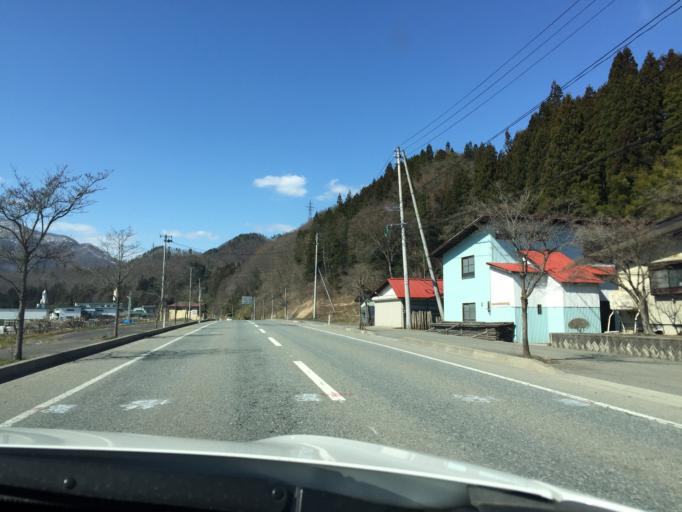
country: JP
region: Yamagata
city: Nagai
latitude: 38.2202
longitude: 140.0988
